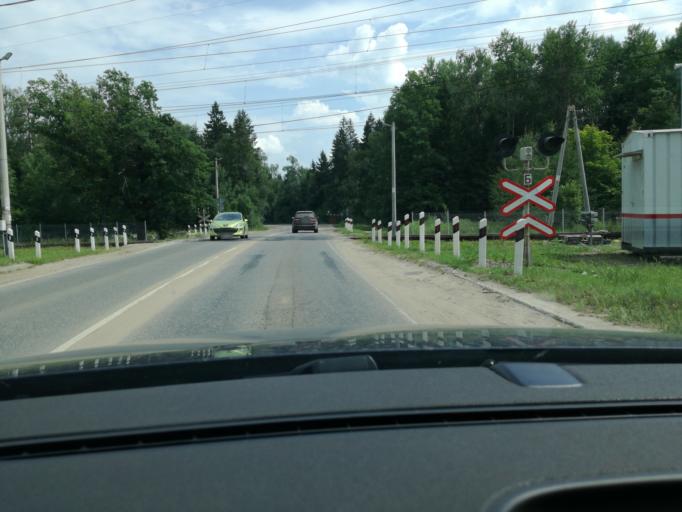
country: RU
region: Moskovskaya
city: Khot'kovo
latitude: 56.3028
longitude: 37.9537
